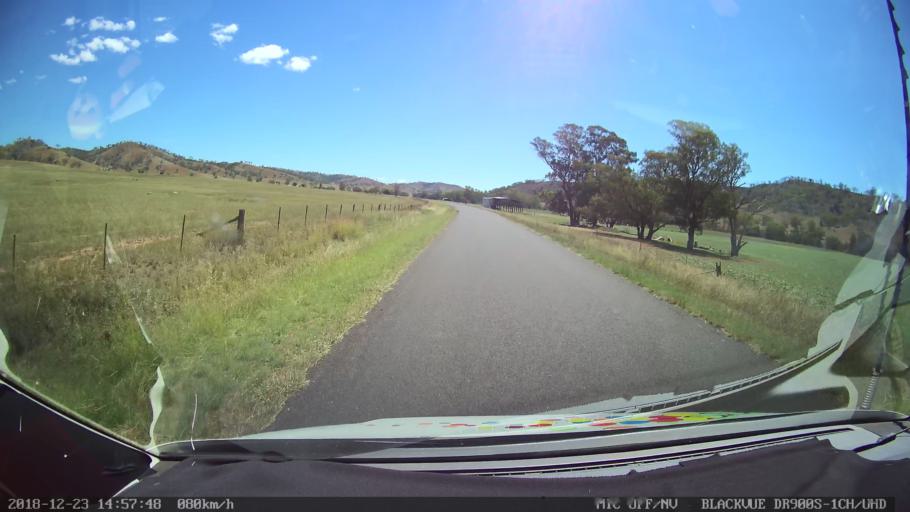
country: AU
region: New South Wales
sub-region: Tamworth Municipality
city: Manilla
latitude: -30.7116
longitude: 150.8199
